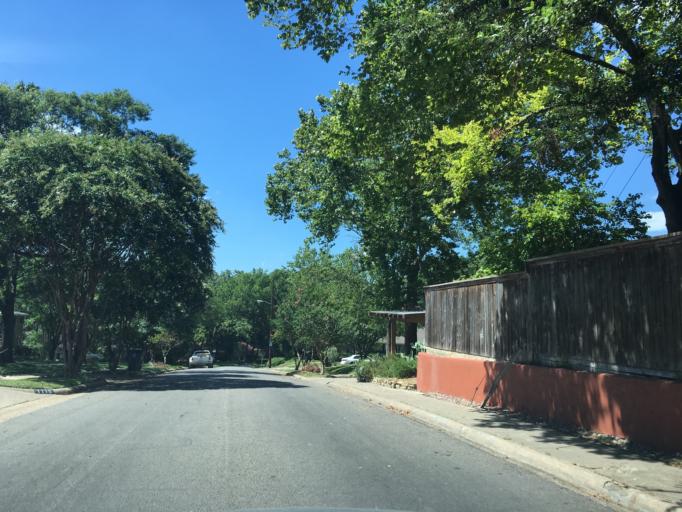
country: US
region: Texas
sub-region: Dallas County
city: Highland Park
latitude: 32.8369
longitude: -96.7036
